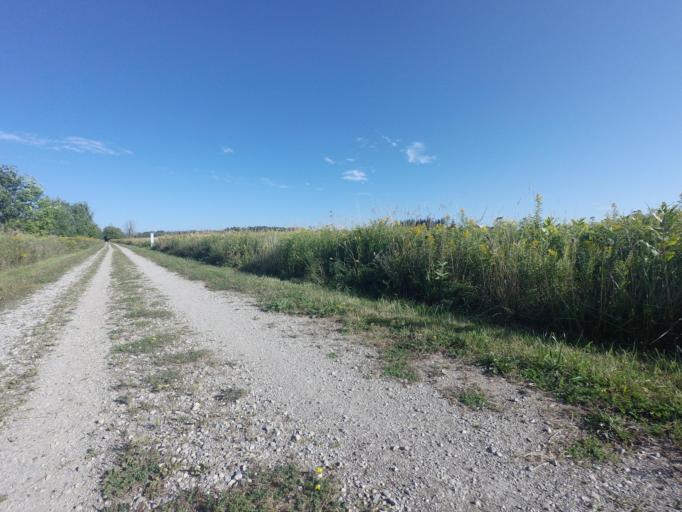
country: CA
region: Ontario
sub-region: Wellington County
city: Guelph
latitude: 43.6595
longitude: -80.4278
